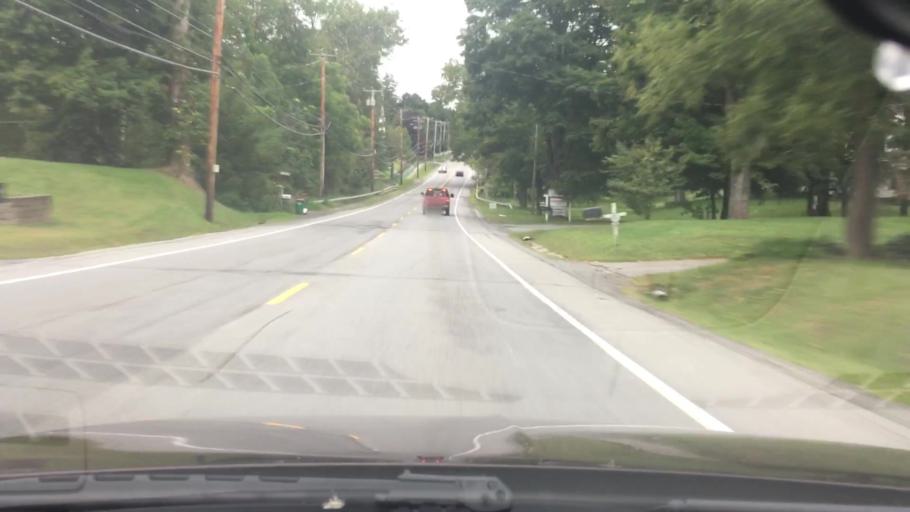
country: US
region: New York
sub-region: Dutchess County
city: Pleasant Valley
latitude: 41.7485
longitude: -73.8136
